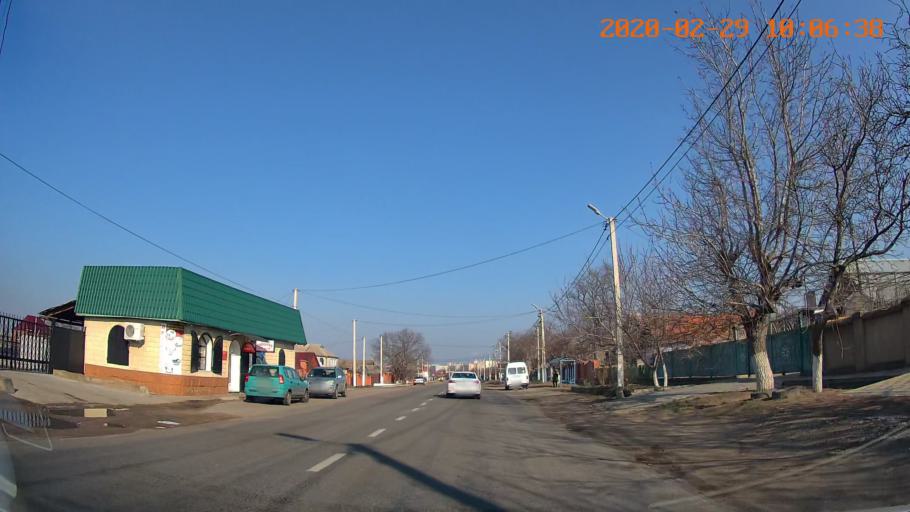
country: MD
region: Telenesti
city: Tiraspolul Nou
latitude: 46.8162
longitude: 29.6689
